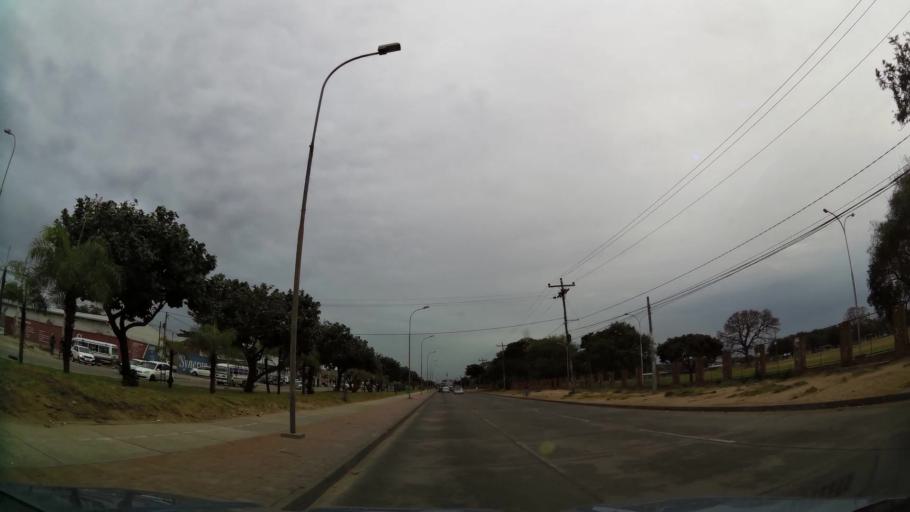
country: BO
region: Santa Cruz
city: Santa Cruz de la Sierra
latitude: -17.8276
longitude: -63.1852
